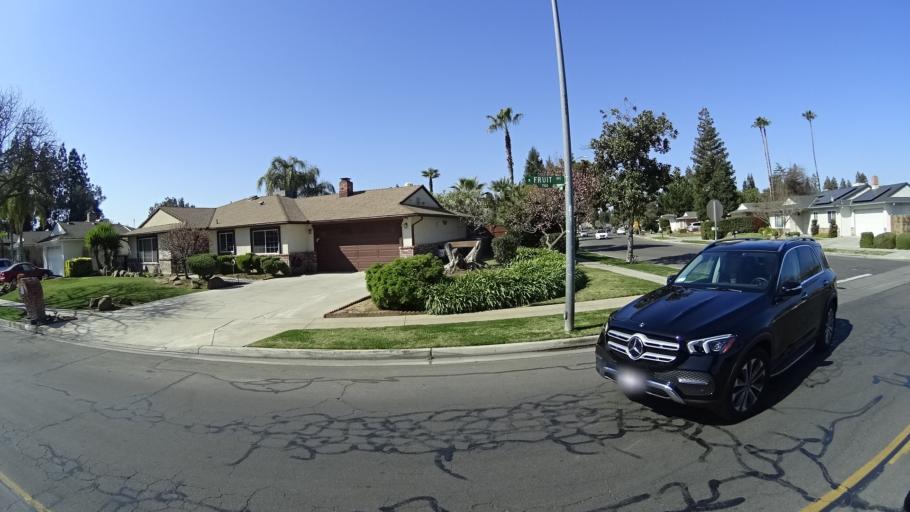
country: US
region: California
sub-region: Fresno County
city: Fresno
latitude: 36.8403
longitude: -119.8177
